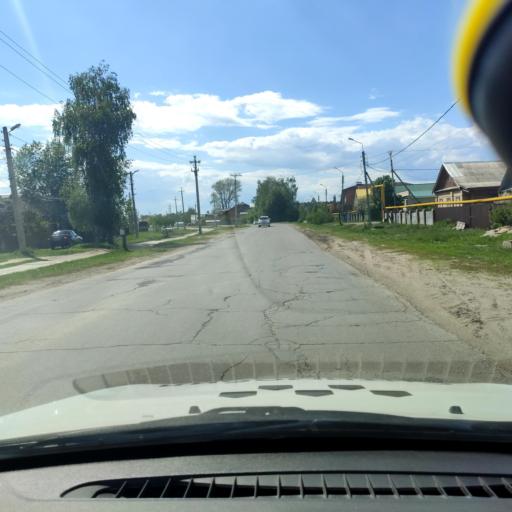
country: RU
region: Samara
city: Zhigulevsk
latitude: 53.4673
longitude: 49.6254
